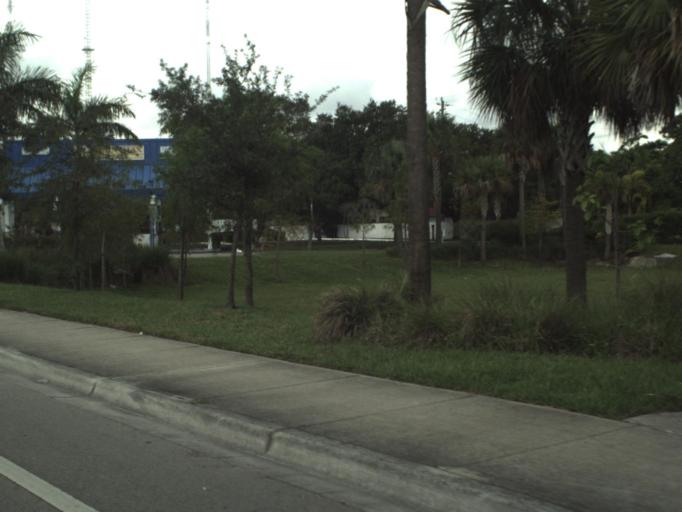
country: US
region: Florida
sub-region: Broward County
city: Miami Gardens
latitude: 25.9767
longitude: -80.2064
